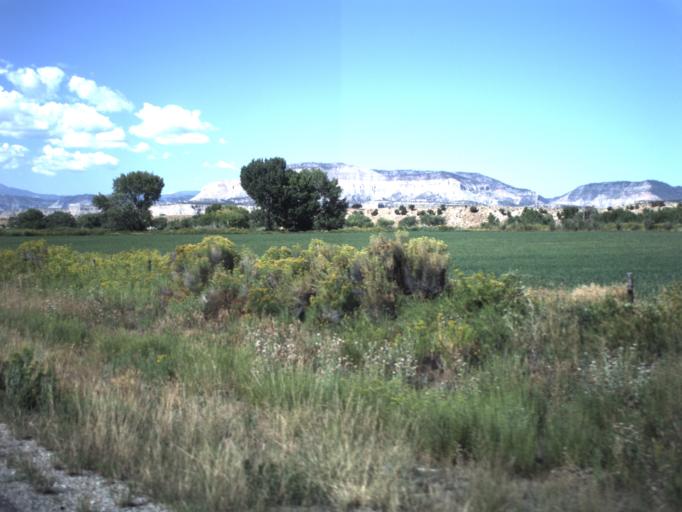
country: US
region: Utah
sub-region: Emery County
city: Ferron
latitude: 38.9048
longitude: -111.2718
